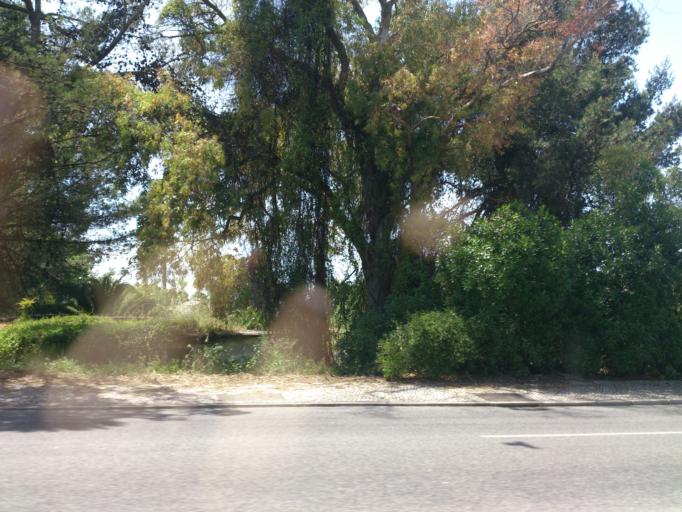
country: PT
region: Lisbon
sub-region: Oeiras
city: Linda-a-Velha
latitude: 38.7013
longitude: -9.2518
